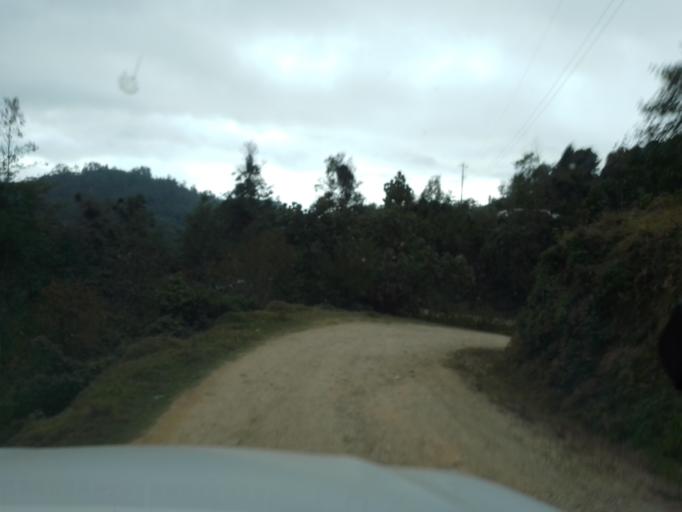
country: MX
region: Chiapas
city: Motozintla de Mendoza
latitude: 15.2188
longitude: -92.2319
